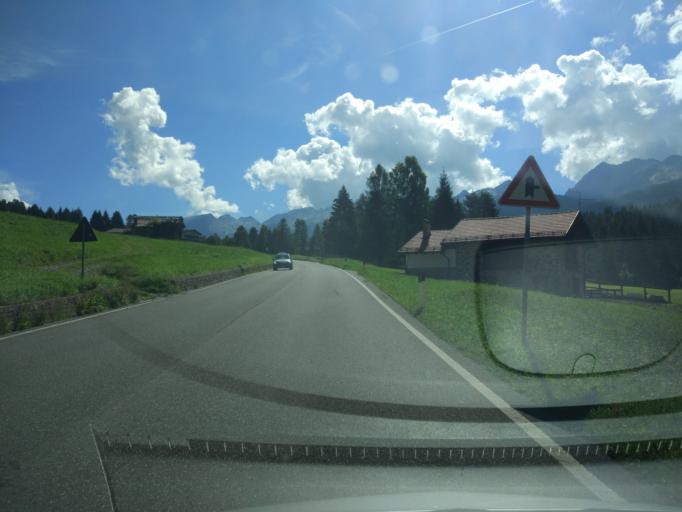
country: IT
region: Trentino-Alto Adige
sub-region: Provincia di Trento
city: Predazzo
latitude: 46.3164
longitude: 11.6545
